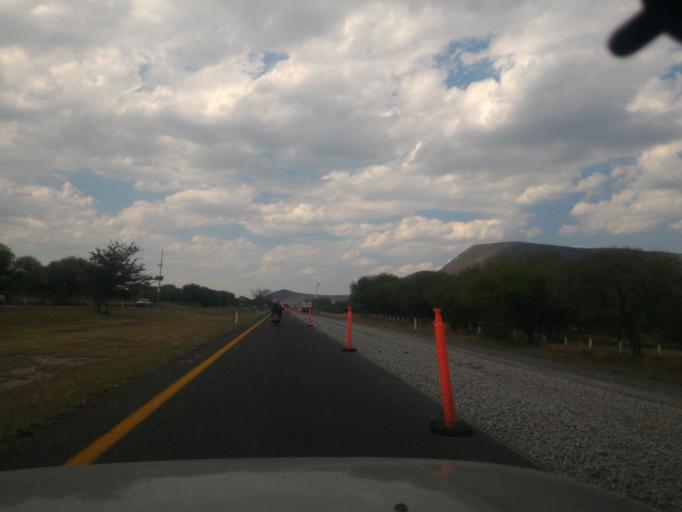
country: MX
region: Jalisco
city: Zacoalco de Torres
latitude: 20.1684
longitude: -103.5049
